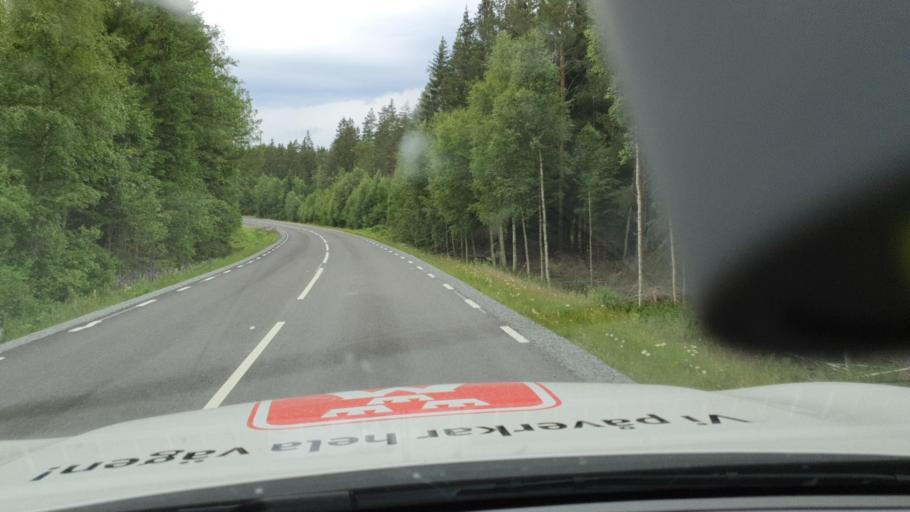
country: SE
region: OErebro
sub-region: Laxa Kommun
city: Laxa
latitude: 58.8728
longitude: 14.5262
